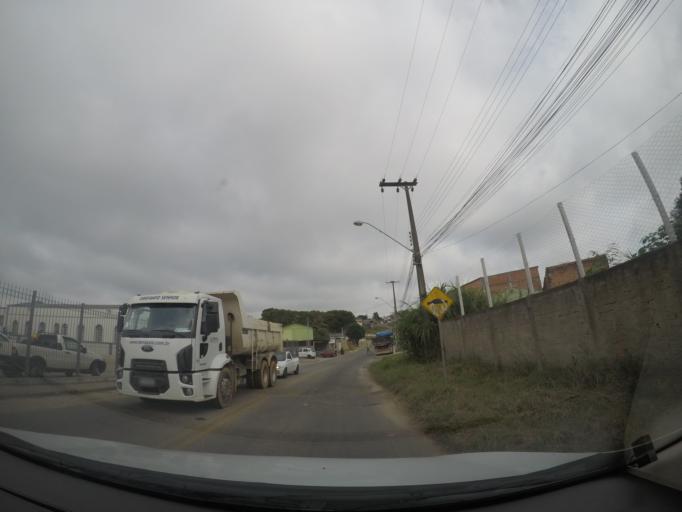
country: BR
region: Parana
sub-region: Colombo
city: Colombo
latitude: -25.3494
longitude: -49.2125
